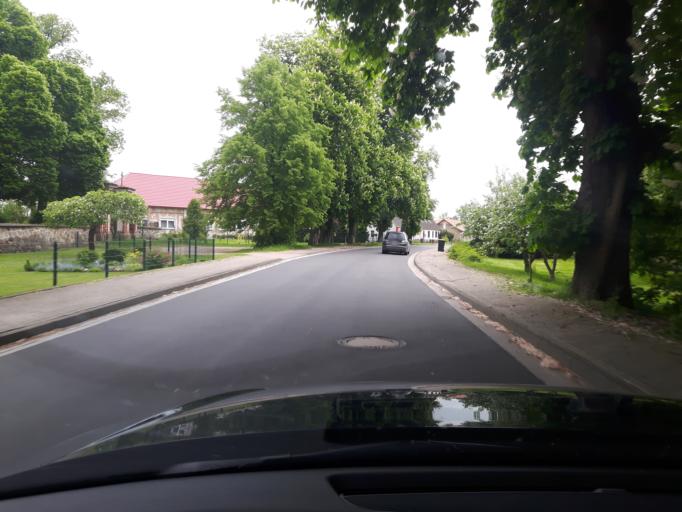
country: DE
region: Mecklenburg-Vorpommern
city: Gnoien
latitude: 54.0294
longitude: 12.6651
